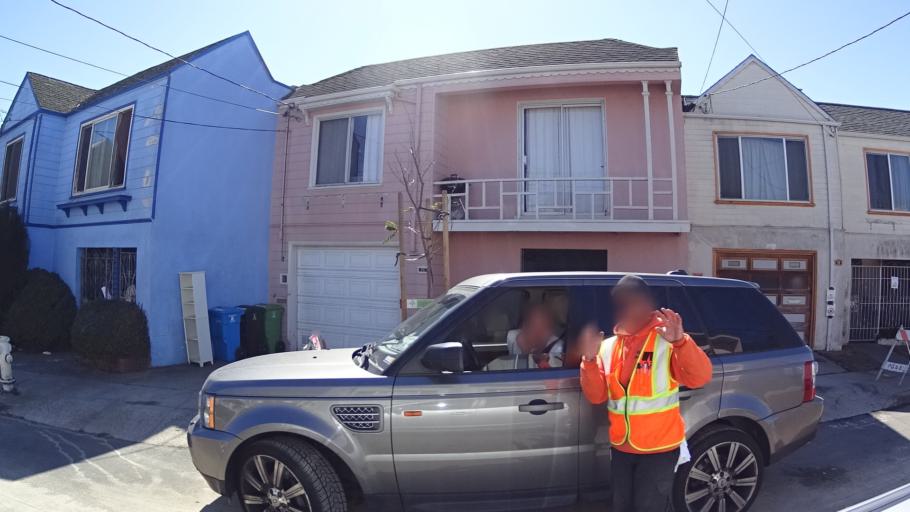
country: US
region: California
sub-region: San Francisco County
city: San Francisco
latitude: 37.7349
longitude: -122.3951
